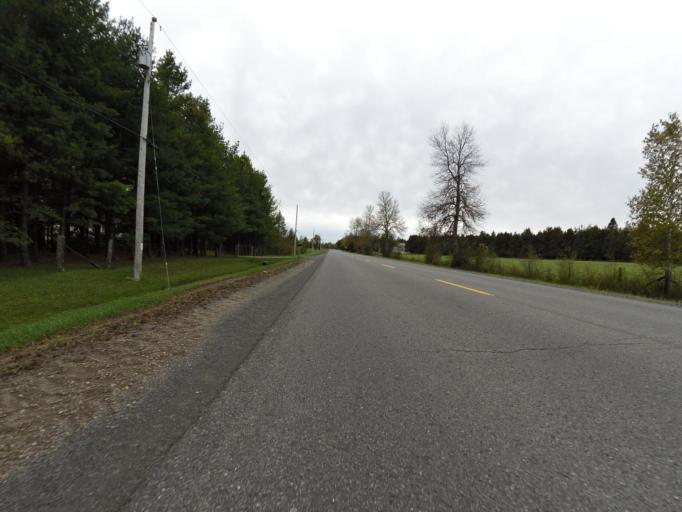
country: CA
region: Ontario
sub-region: Lanark County
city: Smiths Falls
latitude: 44.8450
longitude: -75.8156
